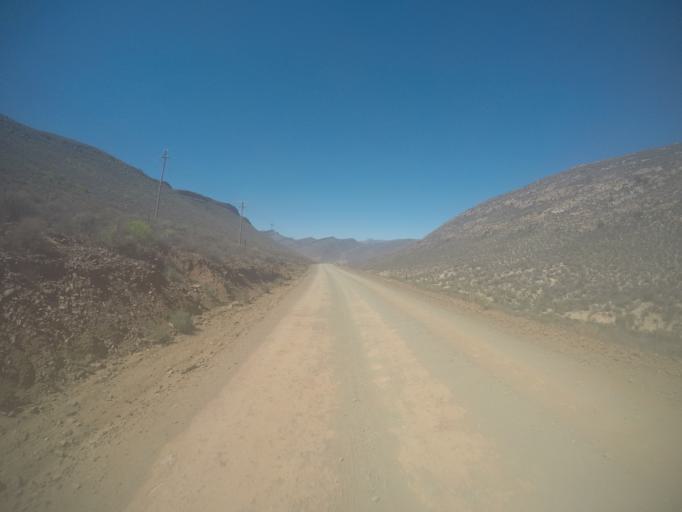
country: ZA
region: Western Cape
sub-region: West Coast District Municipality
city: Clanwilliam
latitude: -32.5342
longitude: 19.3549
